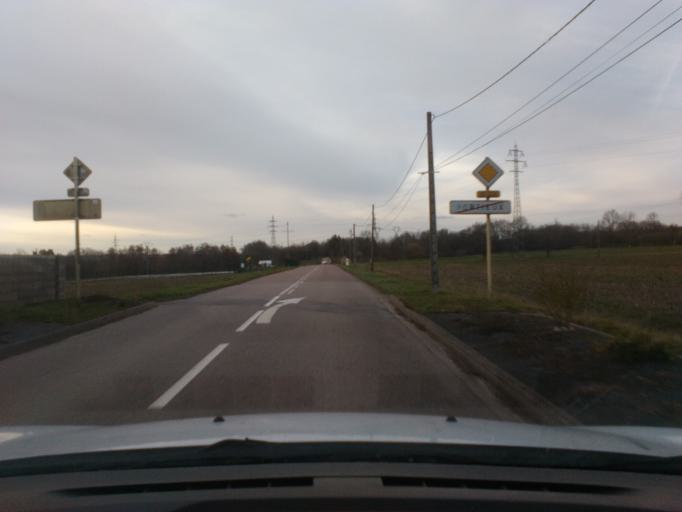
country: FR
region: Lorraine
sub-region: Departement des Vosges
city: Portieux
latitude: 48.3501
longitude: 6.3388
